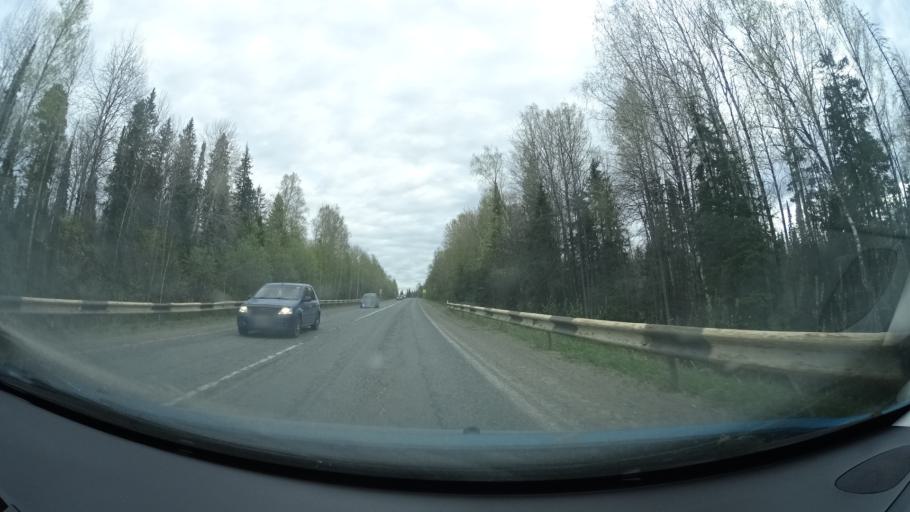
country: RU
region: Perm
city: Yugo-Kamskiy
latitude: 57.6298
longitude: 55.6164
